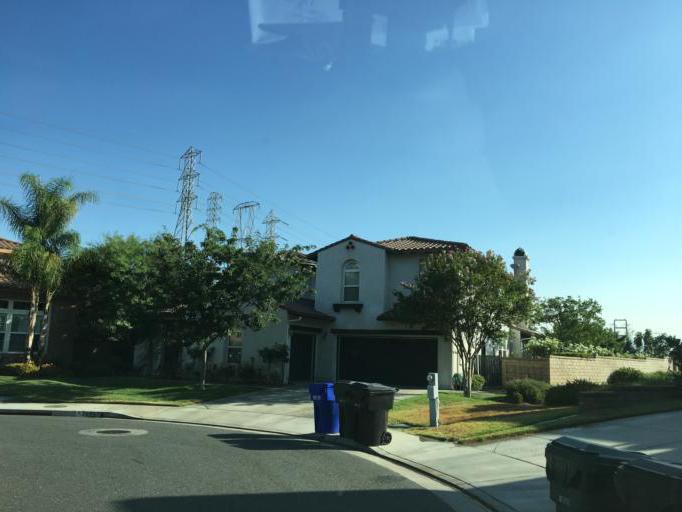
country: US
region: California
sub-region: Los Angeles County
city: Valencia
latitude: 34.4107
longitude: -118.5904
